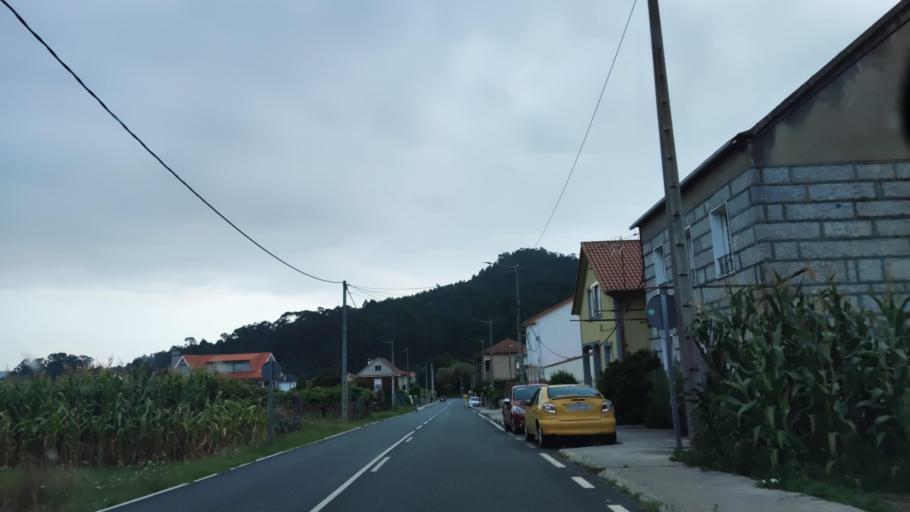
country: ES
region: Galicia
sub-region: Provincia de Pontevedra
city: Catoira
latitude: 42.6685
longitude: -8.7428
